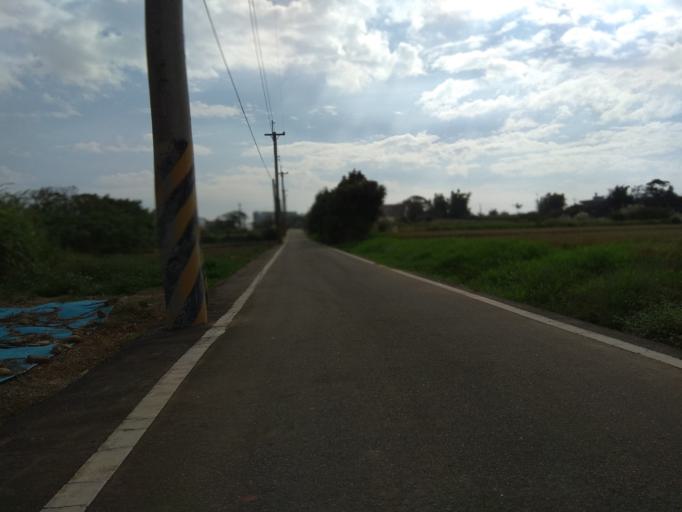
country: TW
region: Taiwan
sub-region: Hsinchu
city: Zhubei
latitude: 24.9502
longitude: 121.0015
